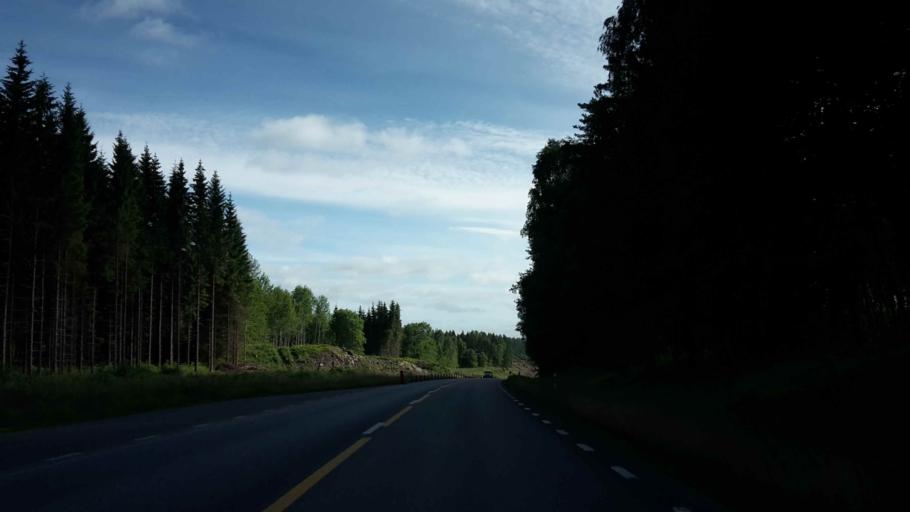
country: SE
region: OErebro
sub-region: Askersunds Kommun
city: Askersund
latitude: 58.9203
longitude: 14.9849
